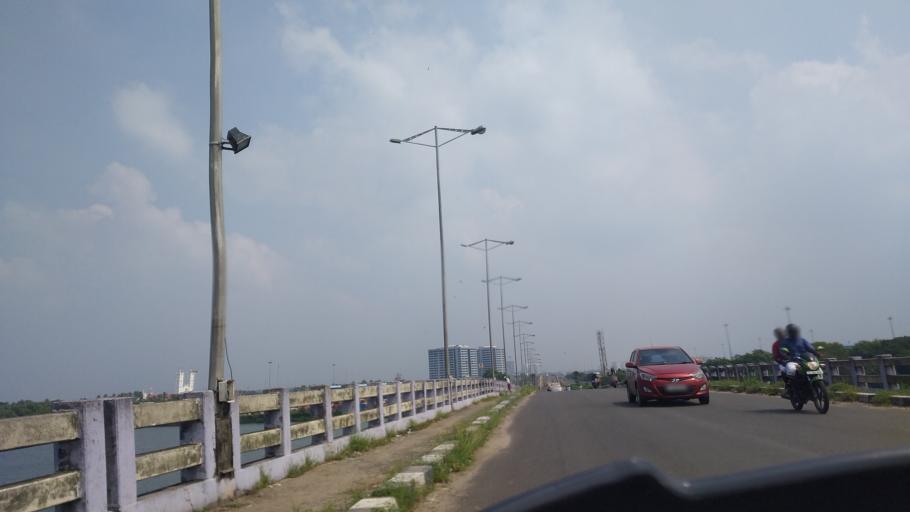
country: IN
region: Kerala
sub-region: Ernakulam
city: Cochin
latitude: 9.9837
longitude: 76.2444
